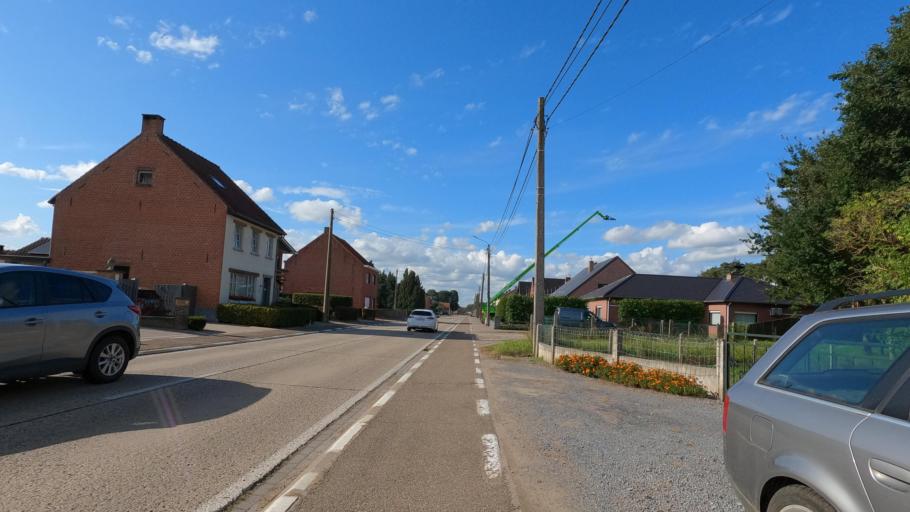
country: BE
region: Flanders
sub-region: Provincie Antwerpen
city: Herselt
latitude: 51.0322
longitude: 4.8928
